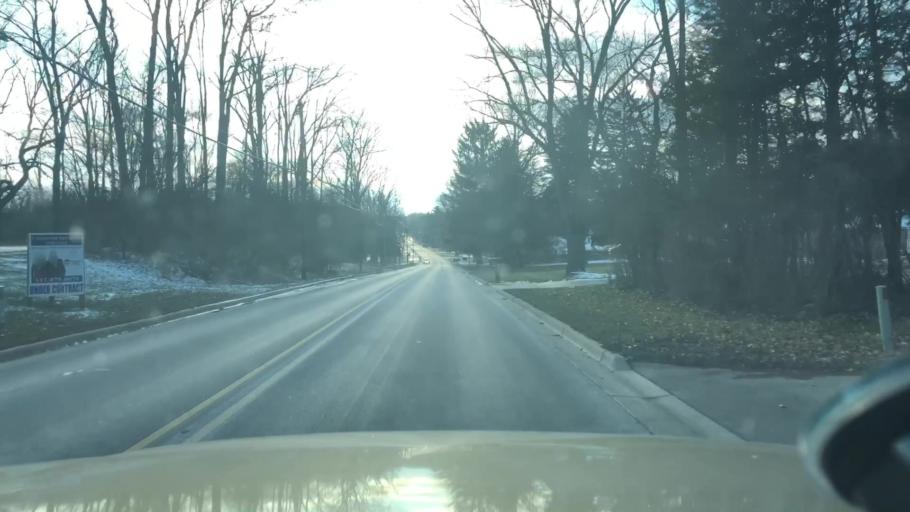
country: US
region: Michigan
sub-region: Jackson County
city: Vandercook Lake
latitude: 42.2098
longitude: -84.4258
